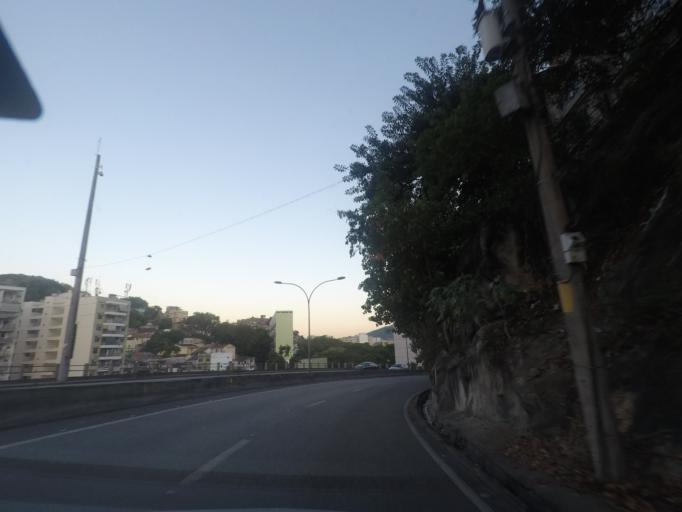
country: BR
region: Rio de Janeiro
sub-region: Rio De Janeiro
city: Rio de Janeiro
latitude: -22.9149
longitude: -43.2643
